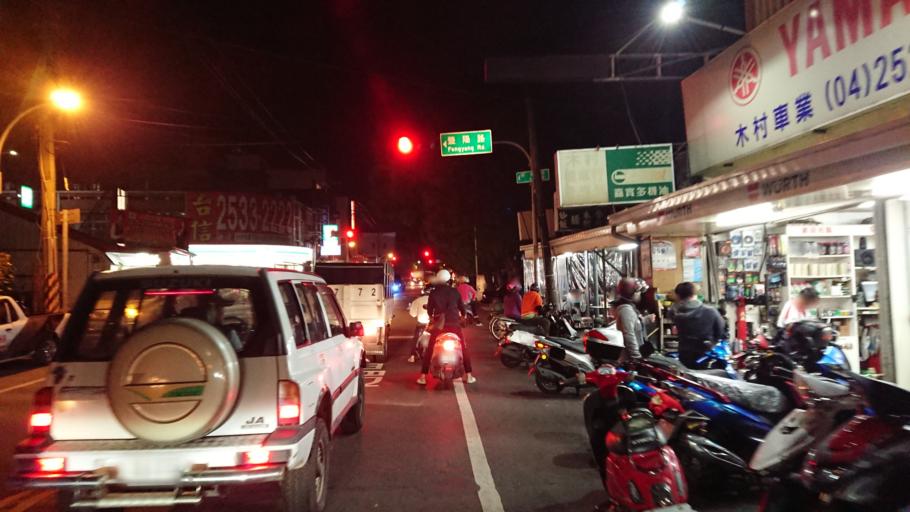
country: TW
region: Taiwan
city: Fengyuan
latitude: 24.2491
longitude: 120.7213
